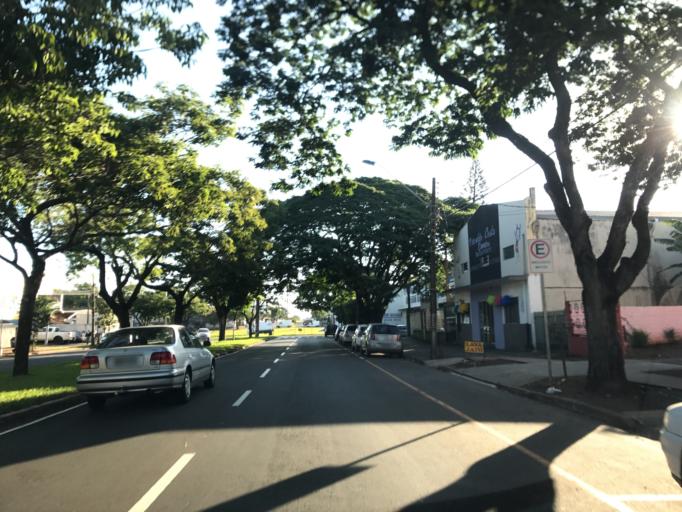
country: BR
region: Parana
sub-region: Maringa
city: Maringa
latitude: -23.4492
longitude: -51.9528
